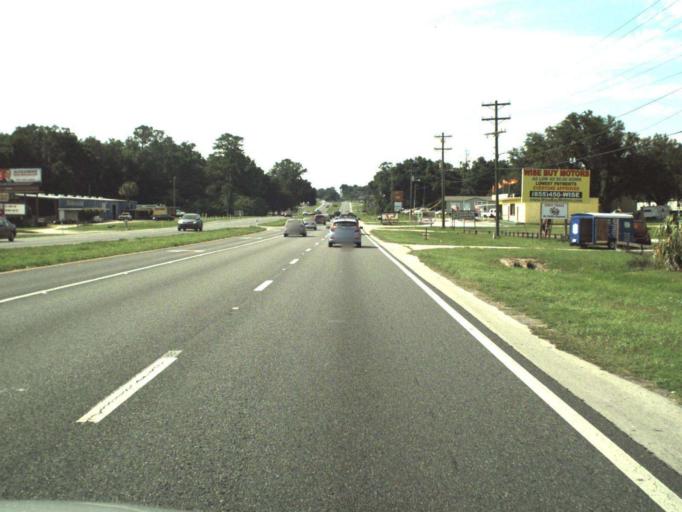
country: US
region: Florida
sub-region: Marion County
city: Ocala
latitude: 29.1382
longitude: -82.1094
